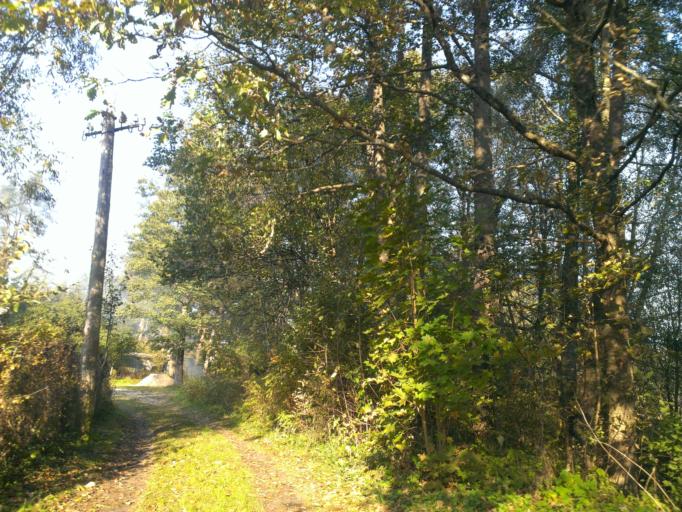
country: LV
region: Garkalne
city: Garkalne
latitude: 57.0449
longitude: 24.4242
